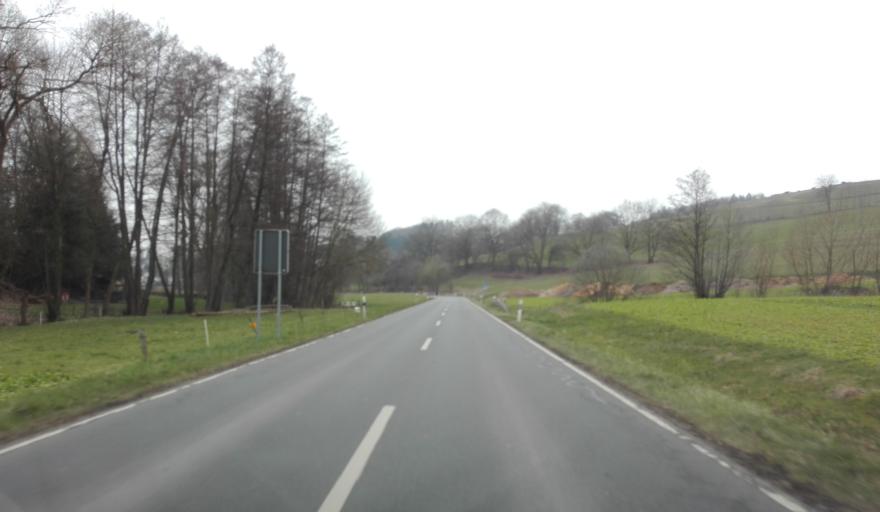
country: DE
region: Hesse
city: Lutzelbach
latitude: 49.7565
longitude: 8.7238
